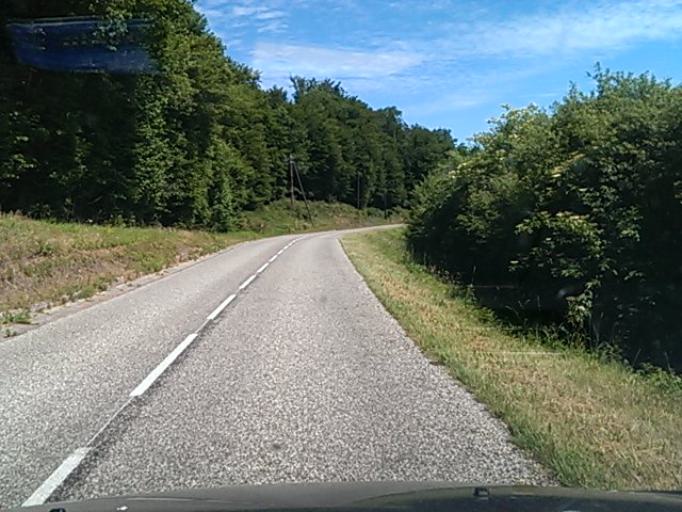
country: FR
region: Alsace
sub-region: Departement du Bas-Rhin
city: Monswiller
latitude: 48.7999
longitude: 7.3279
